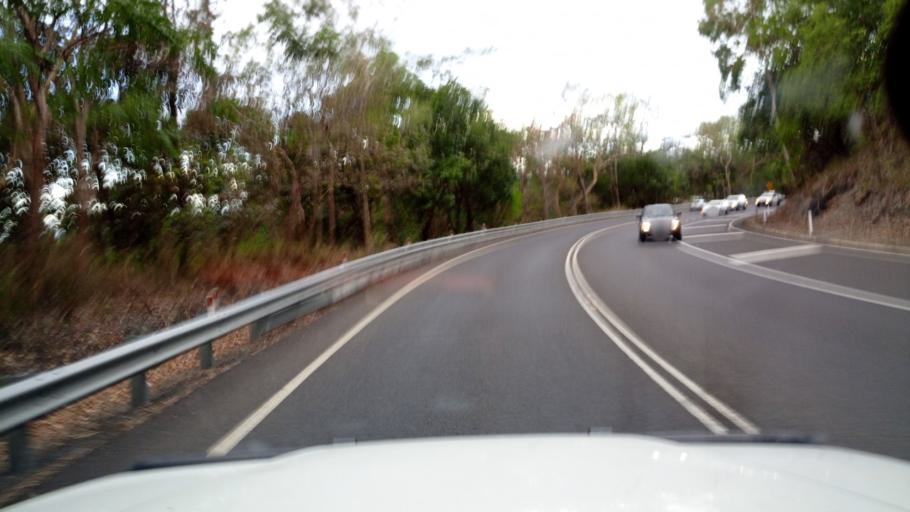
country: AU
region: Queensland
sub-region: Cairns
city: Redlynch
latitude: -16.8371
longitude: 145.6841
